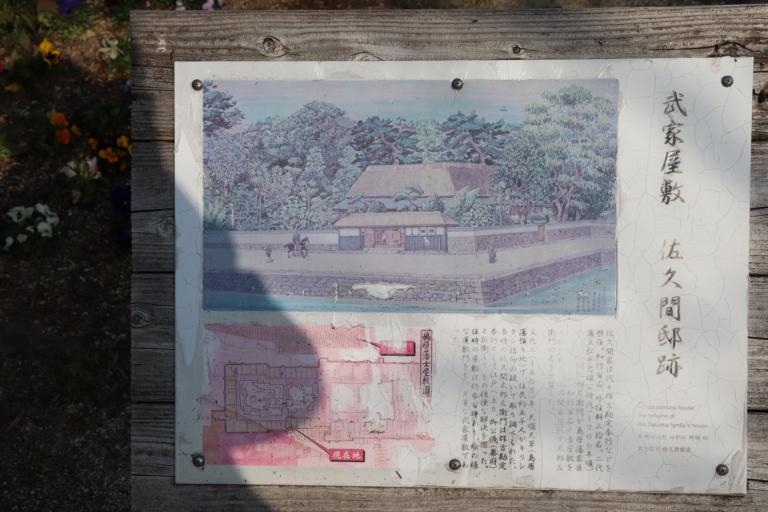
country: JP
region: Nagasaki
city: Shimabara
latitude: 32.7911
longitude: 130.3675
